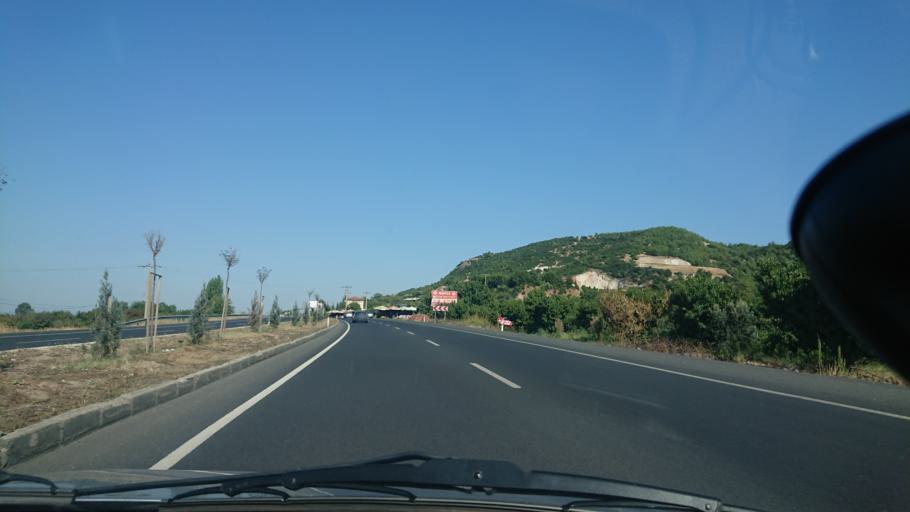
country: TR
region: Manisa
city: Ahmetli
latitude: 38.4846
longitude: 27.8265
